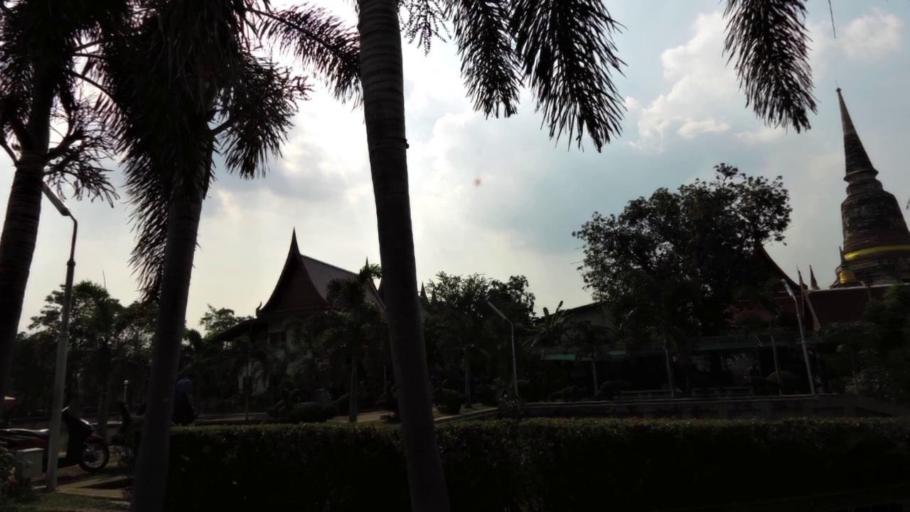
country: TH
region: Phra Nakhon Si Ayutthaya
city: Phra Nakhon Si Ayutthaya
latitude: 14.3452
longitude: 100.5939
